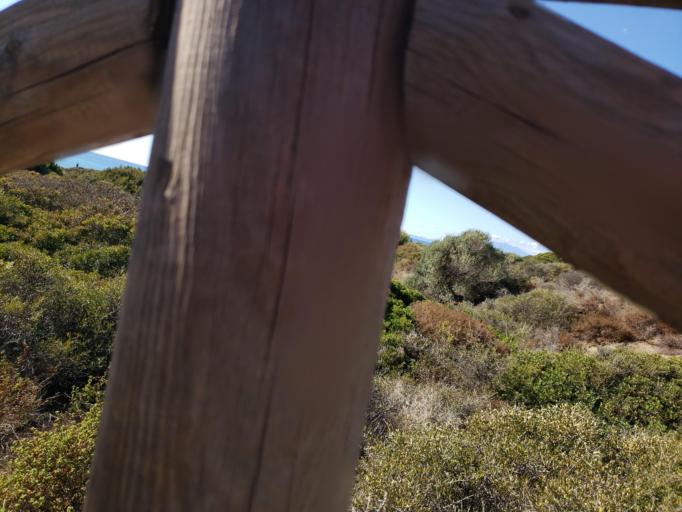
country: ES
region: Andalusia
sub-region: Provincia de Malaga
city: Fuengirola
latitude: 36.4860
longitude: -4.7437
